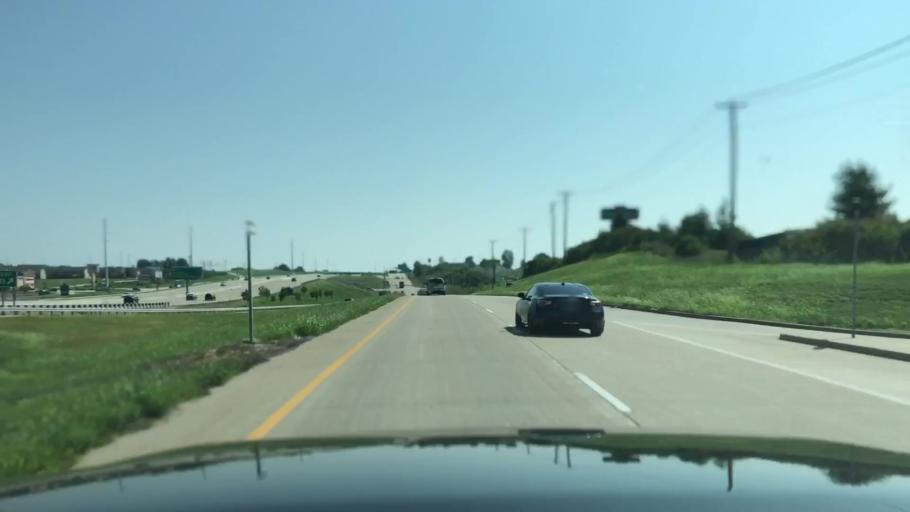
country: US
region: Missouri
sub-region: Saint Charles County
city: Cottleville
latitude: 38.7470
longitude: -90.5894
